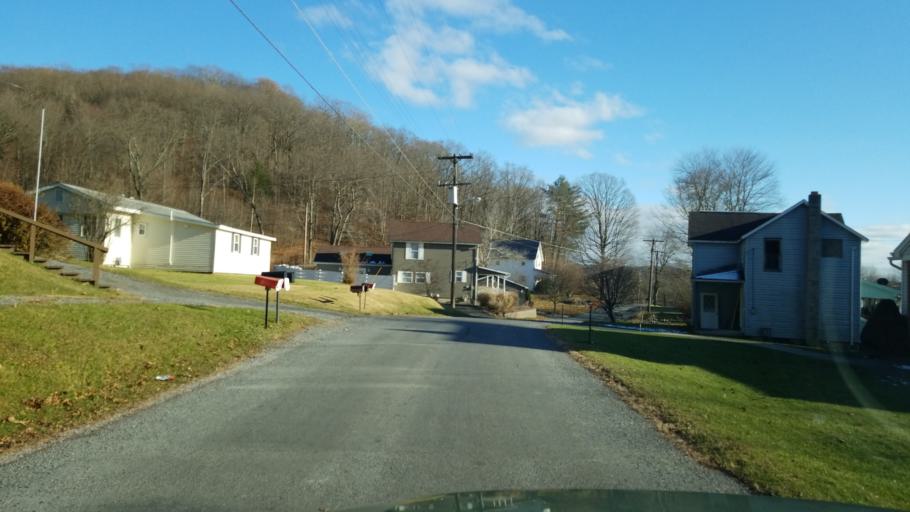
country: US
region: Pennsylvania
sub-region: Jefferson County
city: Brockway
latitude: 41.2554
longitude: -78.7966
